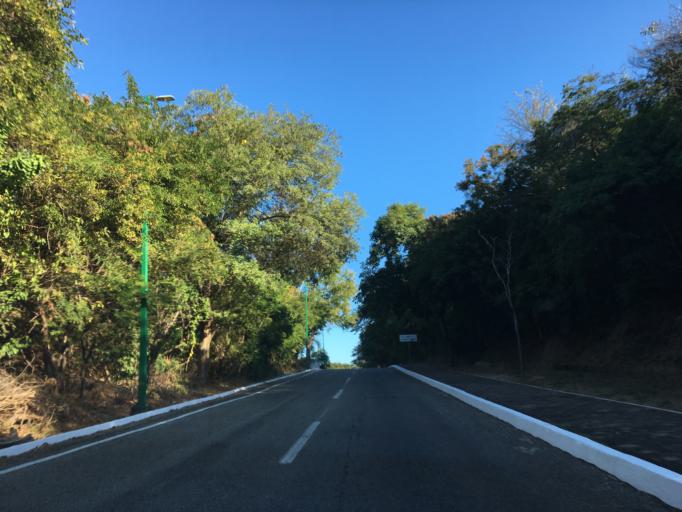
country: MX
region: Oaxaca
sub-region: Santa Maria Huatulco
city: Crucecita
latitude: 15.7765
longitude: -96.0894
